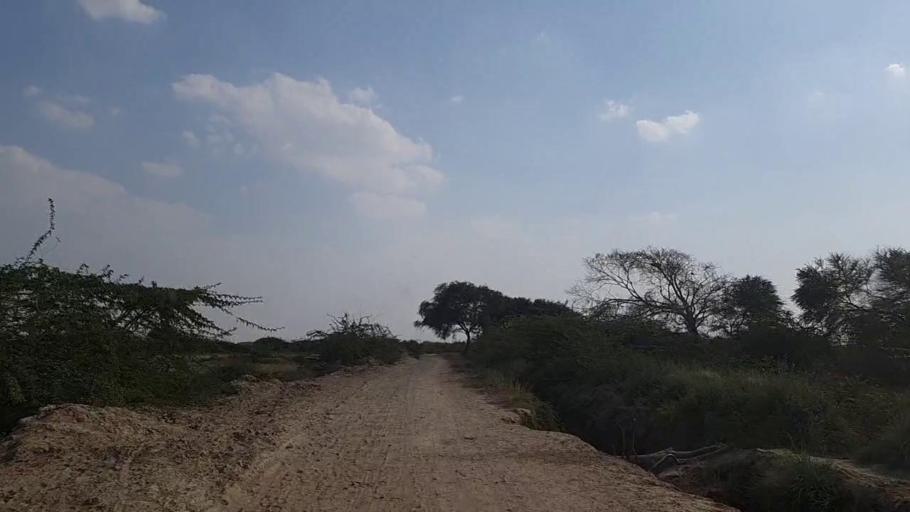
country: PK
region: Sindh
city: Jati
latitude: 24.4870
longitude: 68.3431
